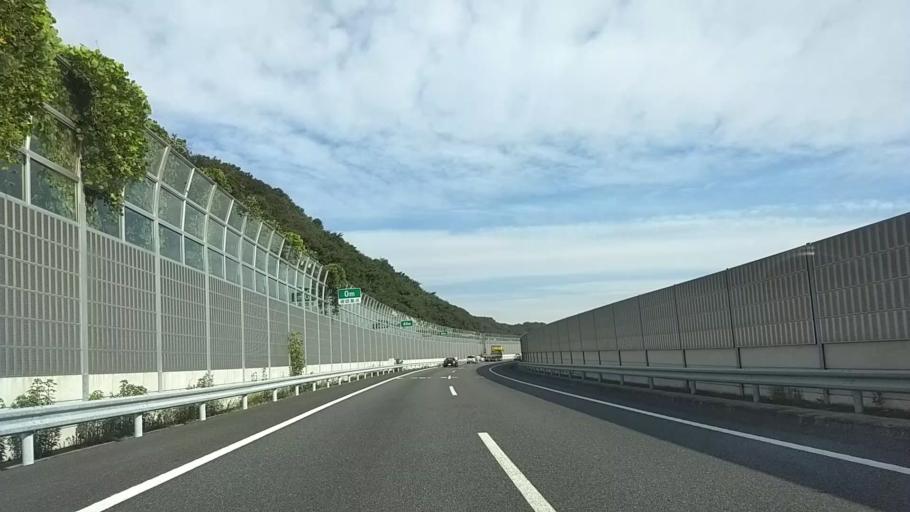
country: JP
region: Kanagawa
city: Zama
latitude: 35.4989
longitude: 139.3659
